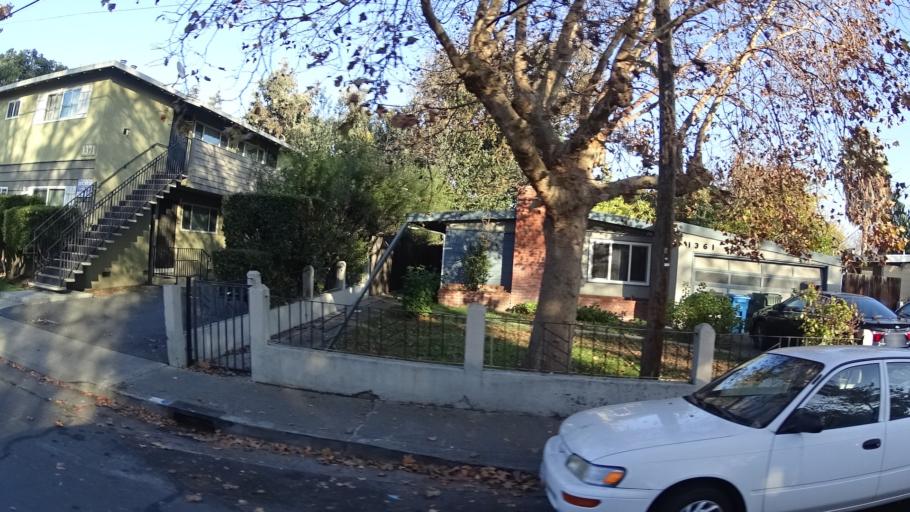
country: US
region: California
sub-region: Santa Clara County
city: Santa Clara
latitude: 37.3500
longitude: -121.9847
